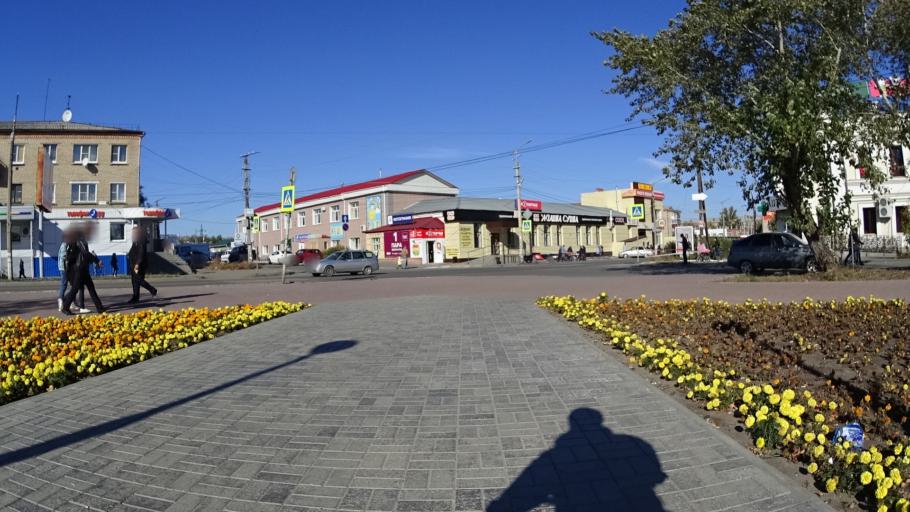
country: RU
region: Chelyabinsk
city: Troitsk
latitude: 54.0883
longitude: 61.5586
